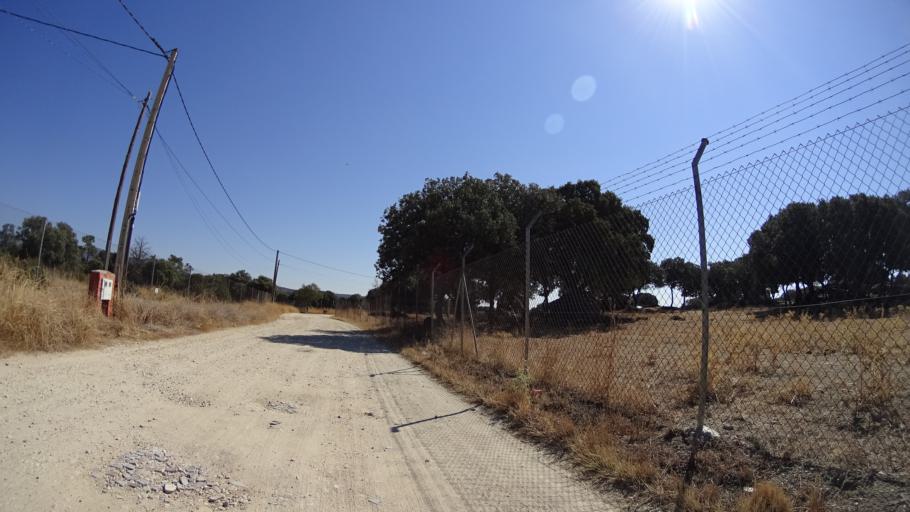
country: ES
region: Madrid
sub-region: Provincia de Madrid
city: Collado-Villalba
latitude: 40.6152
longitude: -4.0007
